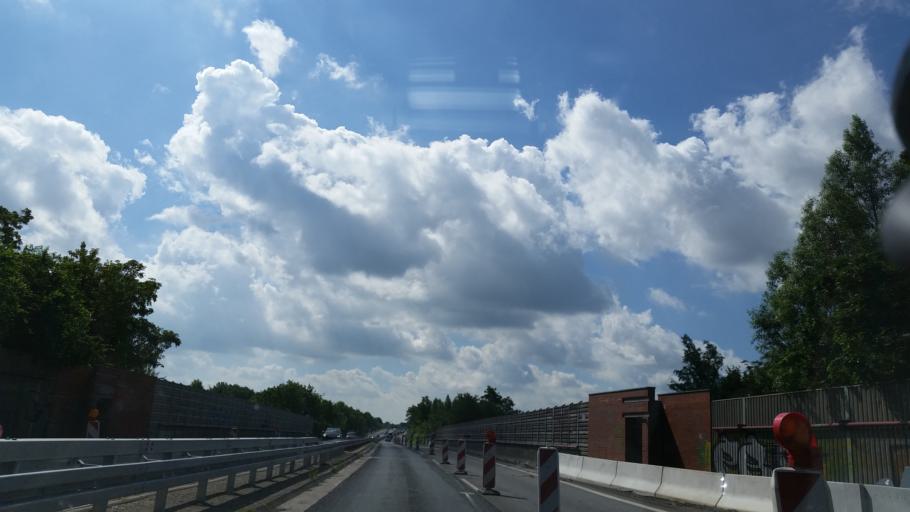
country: DE
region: Lower Saxony
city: Braunschweig
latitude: 52.2611
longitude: 10.4872
